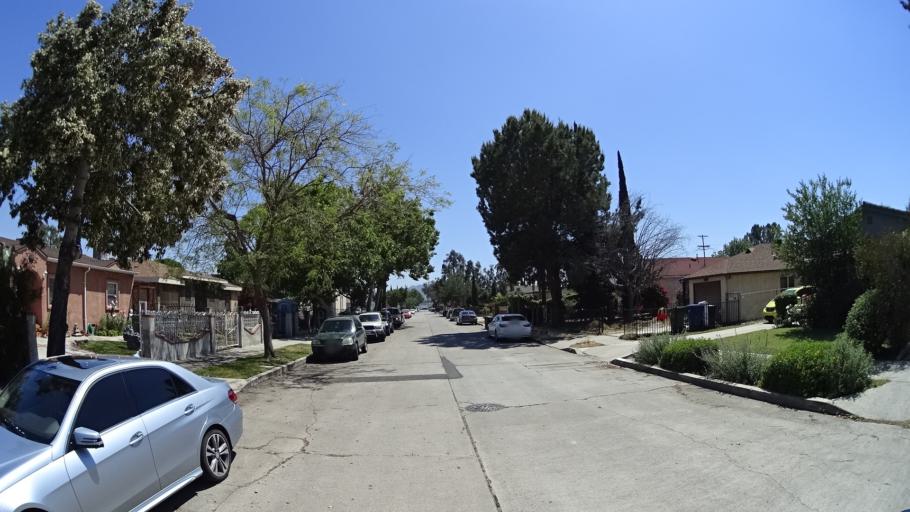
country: US
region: California
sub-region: Los Angeles County
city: North Hollywood
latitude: 34.1748
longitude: -118.3683
